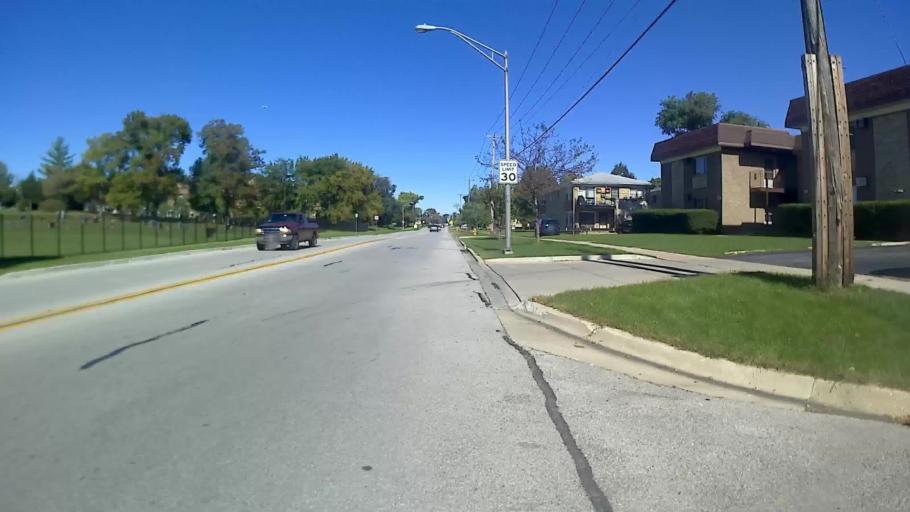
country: US
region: Illinois
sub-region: DuPage County
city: Addison
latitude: 41.9339
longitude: -88.0034
